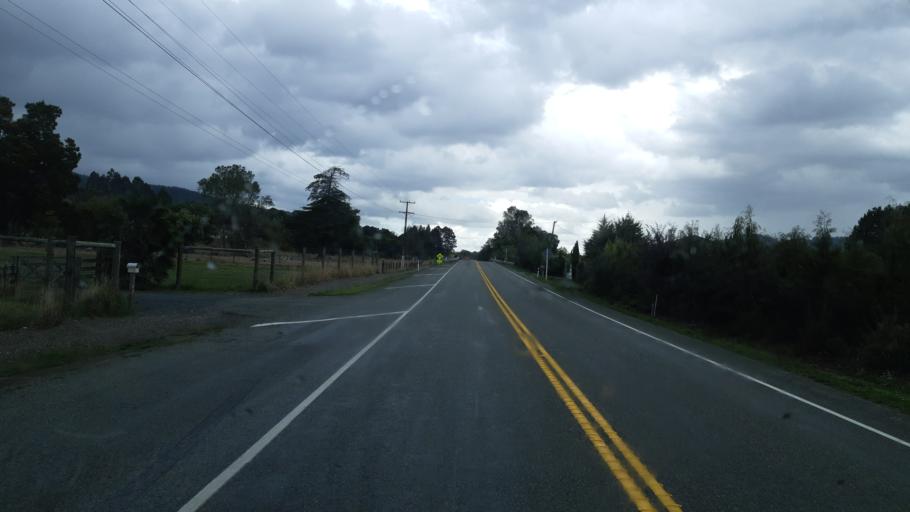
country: NZ
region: Tasman
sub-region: Tasman District
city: Wakefield
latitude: -41.4490
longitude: 172.9600
